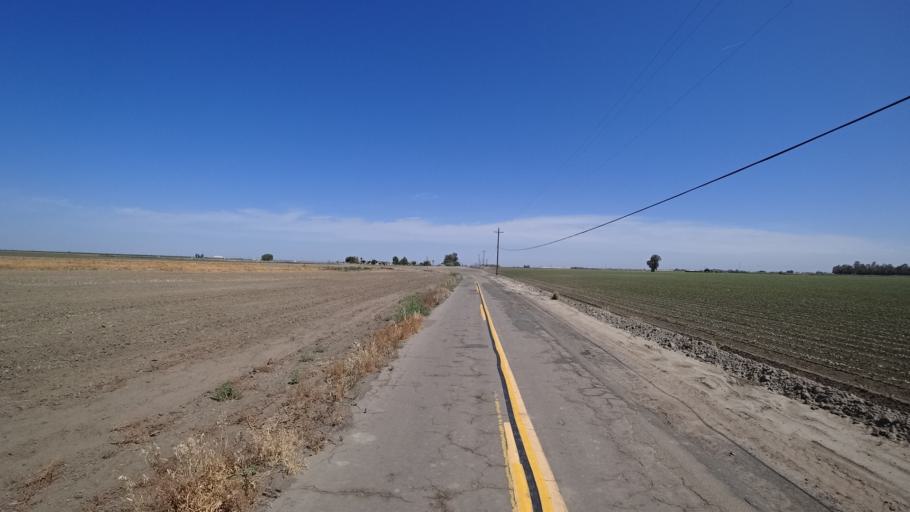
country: US
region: California
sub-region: Kings County
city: Stratford
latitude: 36.2054
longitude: -119.8161
